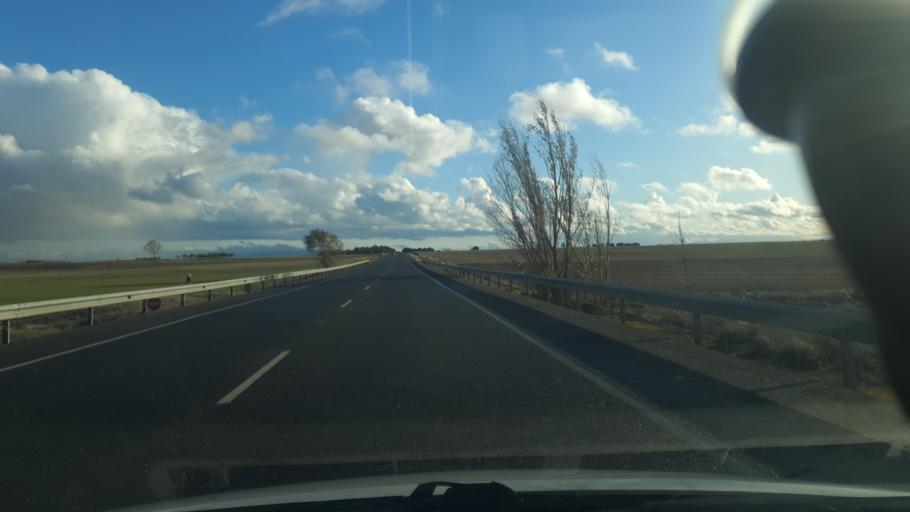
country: ES
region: Castille and Leon
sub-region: Provincia de Segovia
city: Rapariegos
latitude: 41.0792
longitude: -4.6350
